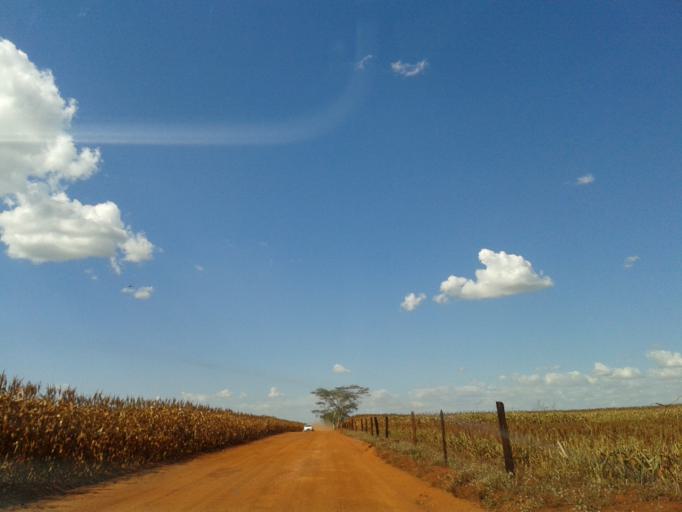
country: BR
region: Minas Gerais
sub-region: Capinopolis
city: Capinopolis
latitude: -18.5994
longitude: -49.5141
